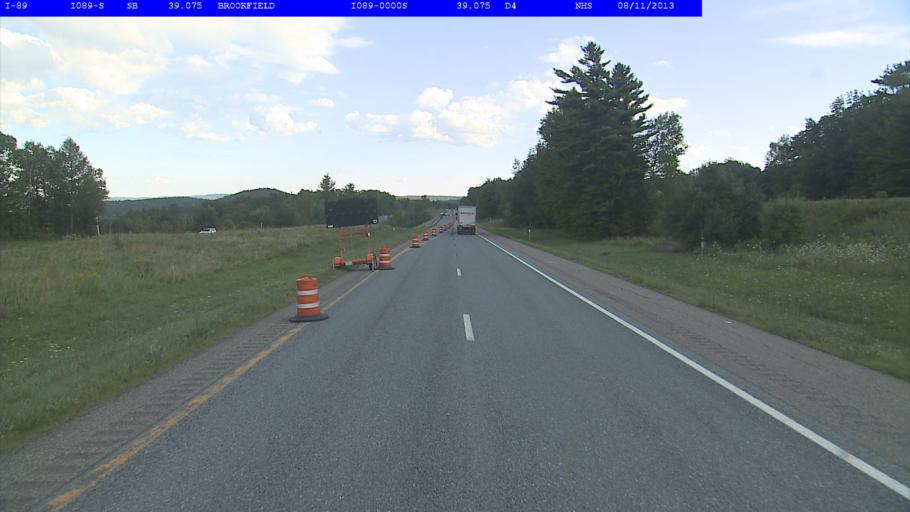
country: US
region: Vermont
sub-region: Orange County
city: Williamstown
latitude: 44.0609
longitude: -72.6065
